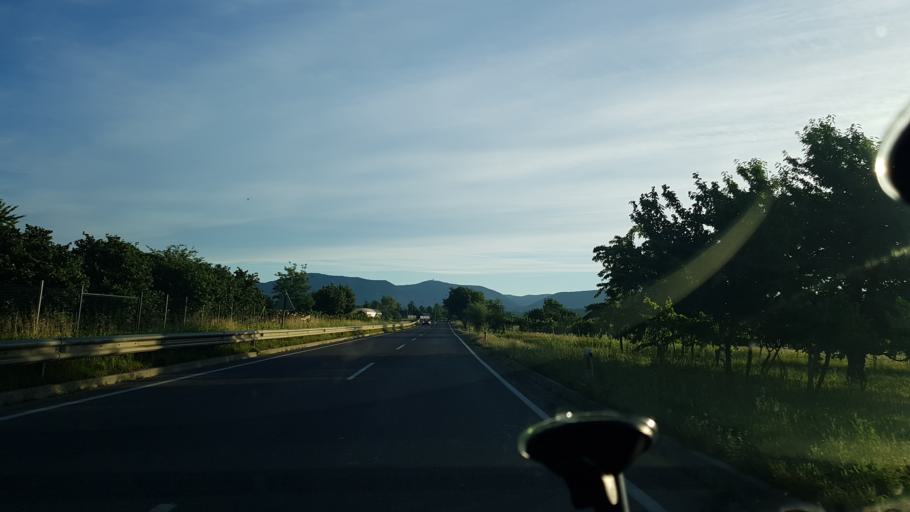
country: SI
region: Sempeter-Vrtojba
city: Vrtojba
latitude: 45.9149
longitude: 13.6287
